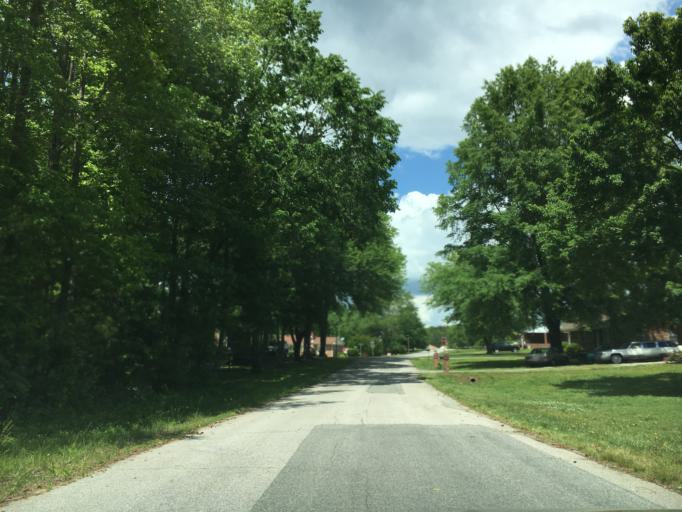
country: US
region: Virginia
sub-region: Halifax County
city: Halifax
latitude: 36.7232
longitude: -78.9447
